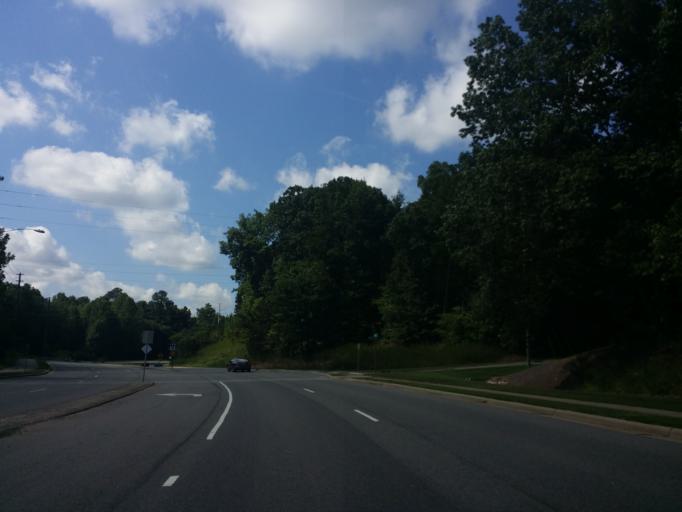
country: US
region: North Carolina
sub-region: Wake County
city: West Raleigh
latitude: 35.8658
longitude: -78.6972
